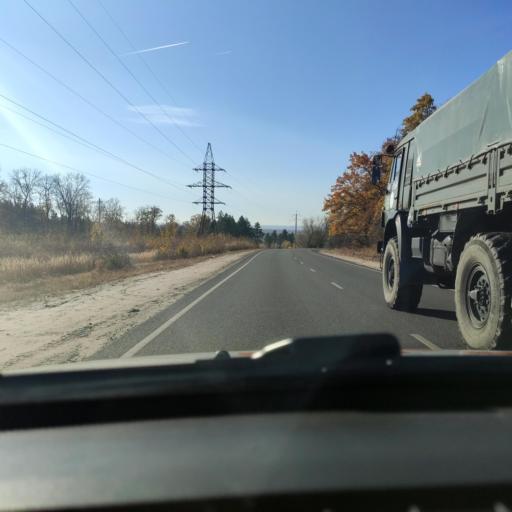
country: RU
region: Voronezj
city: Shilovo
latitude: 51.5591
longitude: 39.1371
